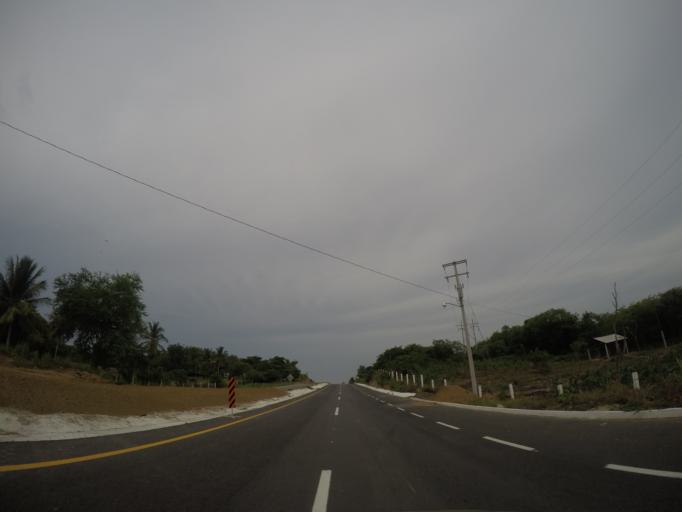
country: MX
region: Oaxaca
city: Santa Maria Tonameca
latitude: 15.7240
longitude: -96.6260
